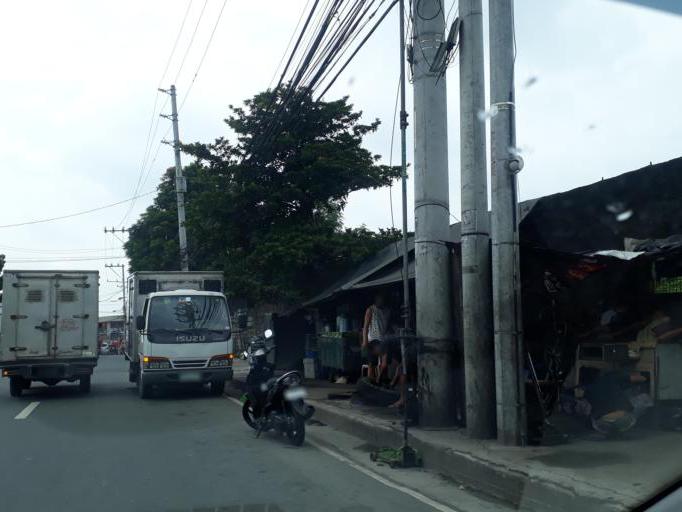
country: PH
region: Calabarzon
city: Del Monte
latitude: 14.6422
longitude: 121.0166
